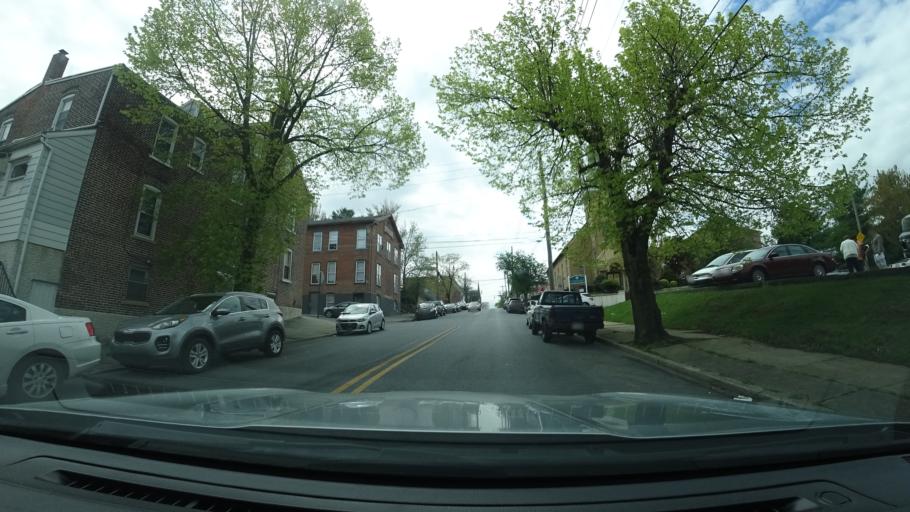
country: US
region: Pennsylvania
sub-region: Lehigh County
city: Fullerton
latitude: 40.6167
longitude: -75.4630
